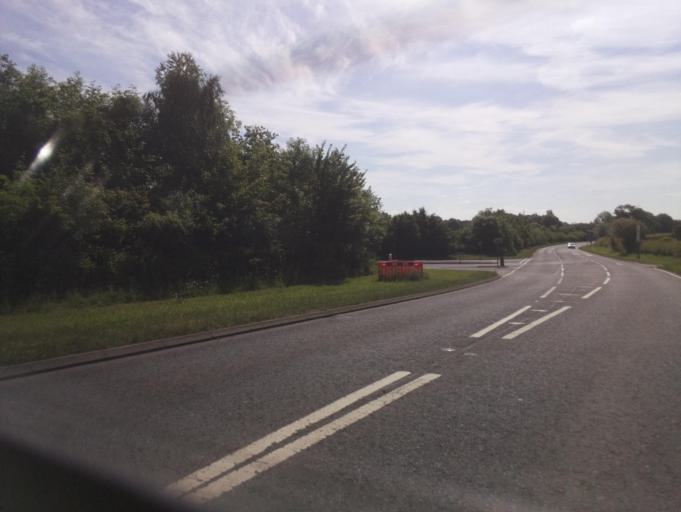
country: GB
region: England
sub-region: Lincolnshire
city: Skellingthorpe
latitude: 53.1669
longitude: -0.6424
